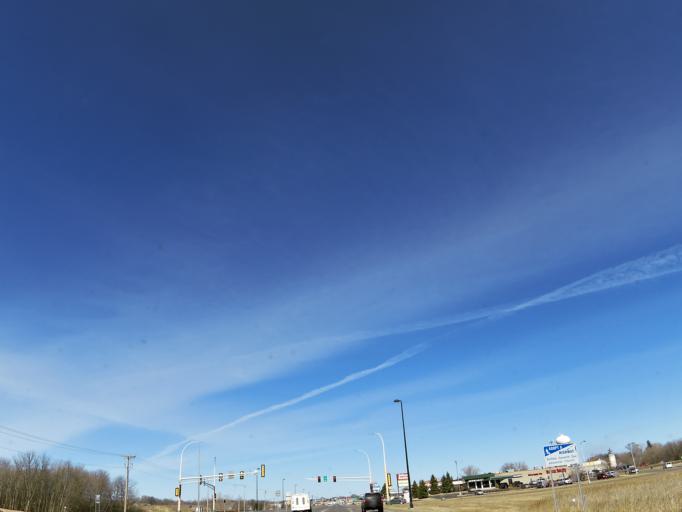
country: US
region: Minnesota
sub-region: Wright County
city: Buffalo
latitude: 45.1641
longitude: -93.8581
